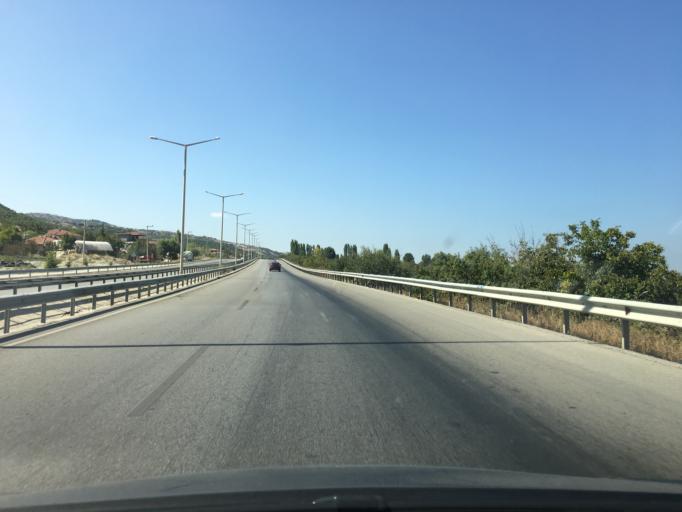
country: TR
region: Burdur
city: Burdur
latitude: 37.7631
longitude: 30.3477
